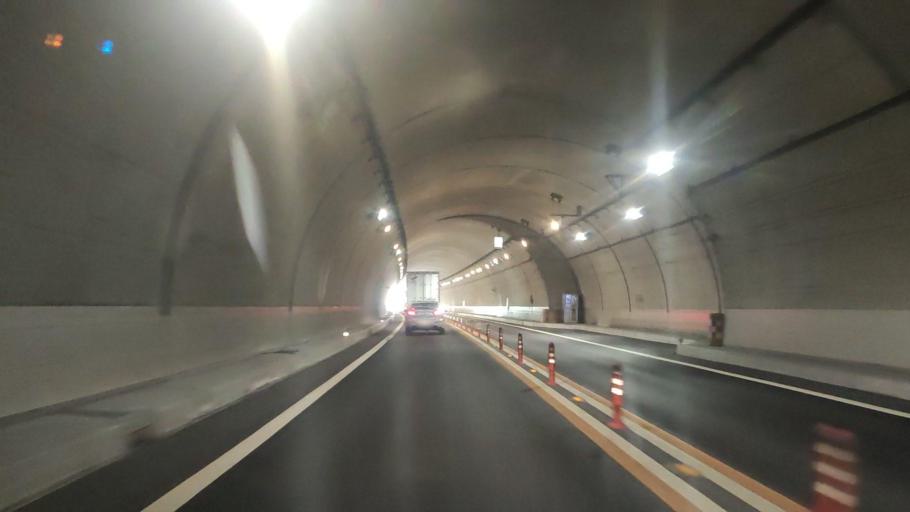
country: JP
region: Fukuoka
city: Kanda
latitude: 33.7752
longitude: 130.9695
